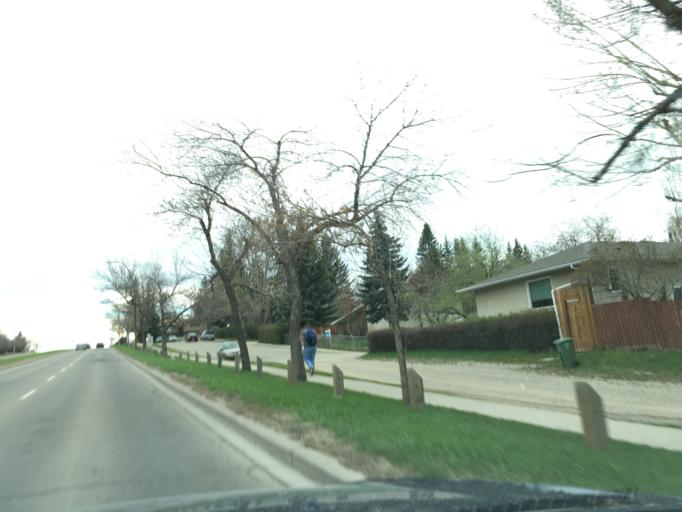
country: CA
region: Alberta
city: Calgary
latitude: 50.9629
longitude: -114.0884
